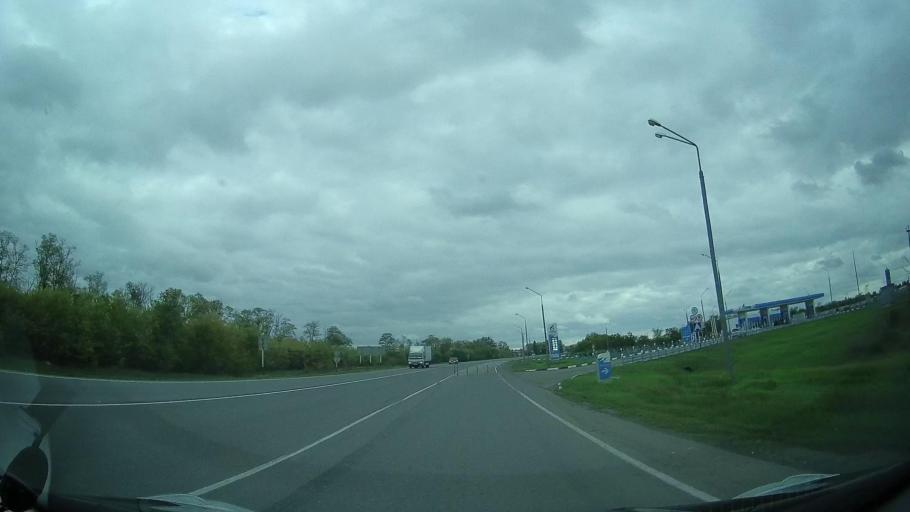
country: RU
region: Rostov
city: Mechetinskaya
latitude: 46.7564
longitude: 40.4541
